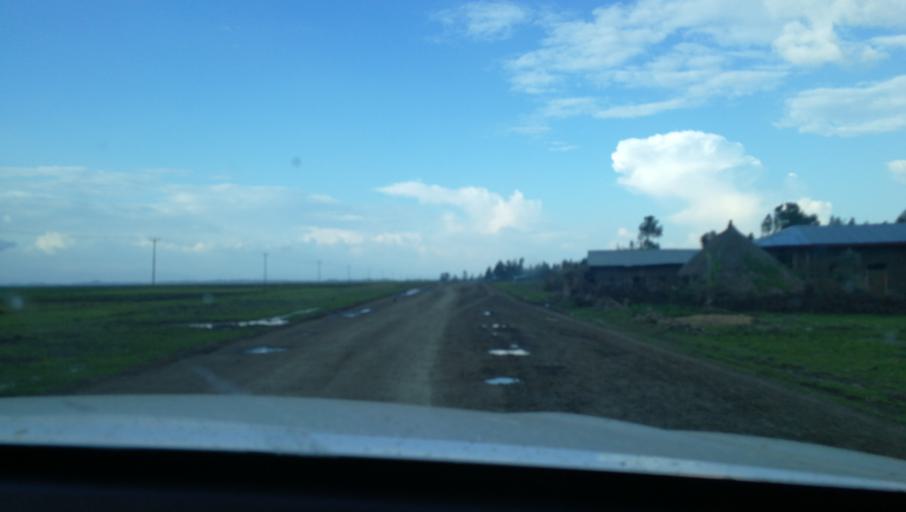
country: ET
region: Amhara
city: Were Ilu
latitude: 10.4425
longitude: 39.2567
